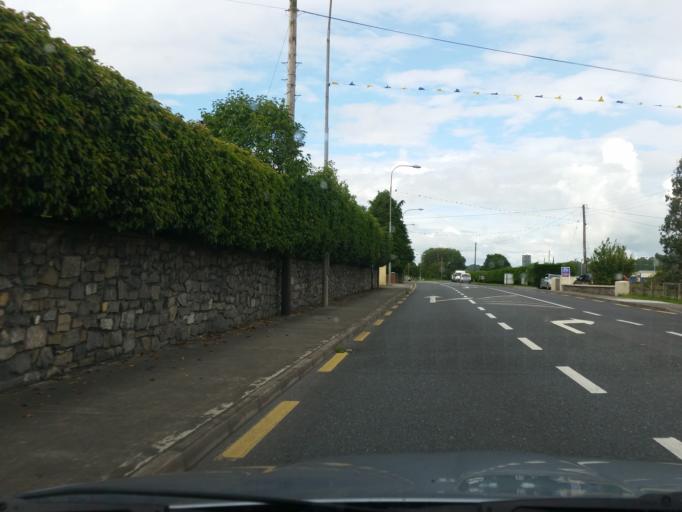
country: IE
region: Ulster
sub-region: An Cabhan
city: Cavan
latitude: 54.0465
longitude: -7.3765
